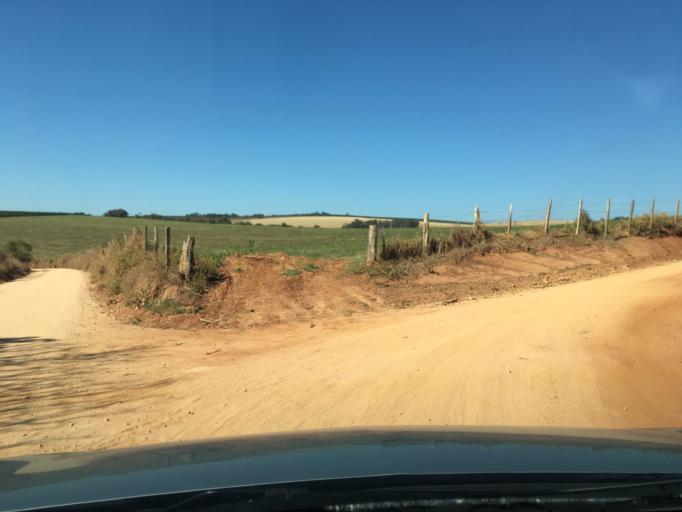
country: BR
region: Minas Gerais
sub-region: Campestre
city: Campestre
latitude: -21.5672
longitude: -46.1955
